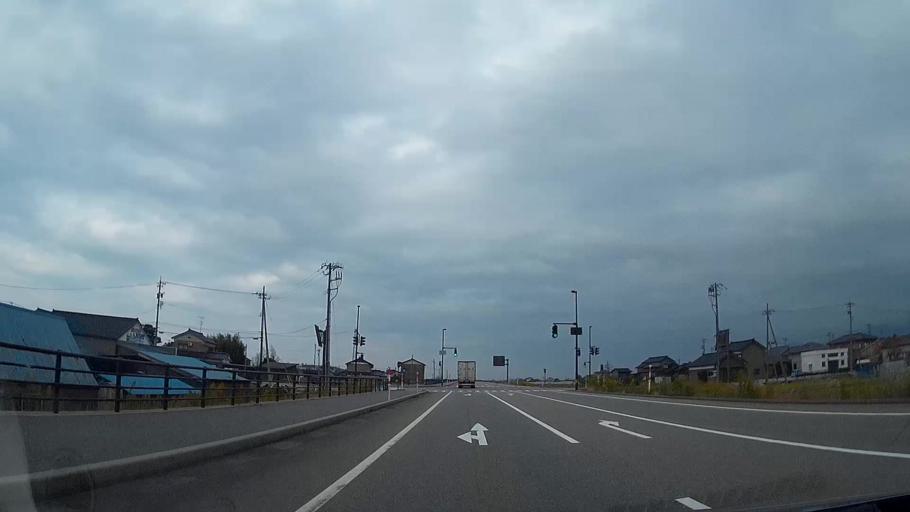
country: JP
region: Toyama
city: Nyuzen
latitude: 36.9204
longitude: 137.4663
